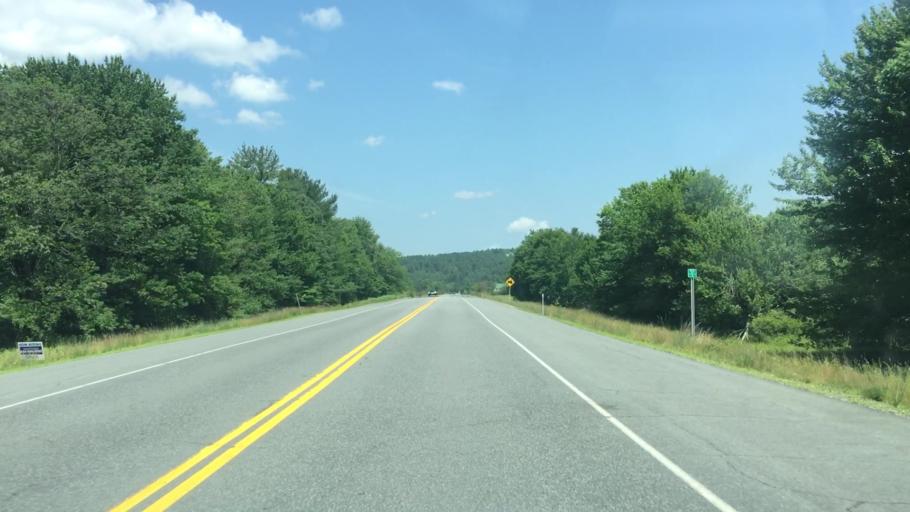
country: US
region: New Hampshire
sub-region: Sullivan County
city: Grantham
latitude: 43.4661
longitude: -72.1470
